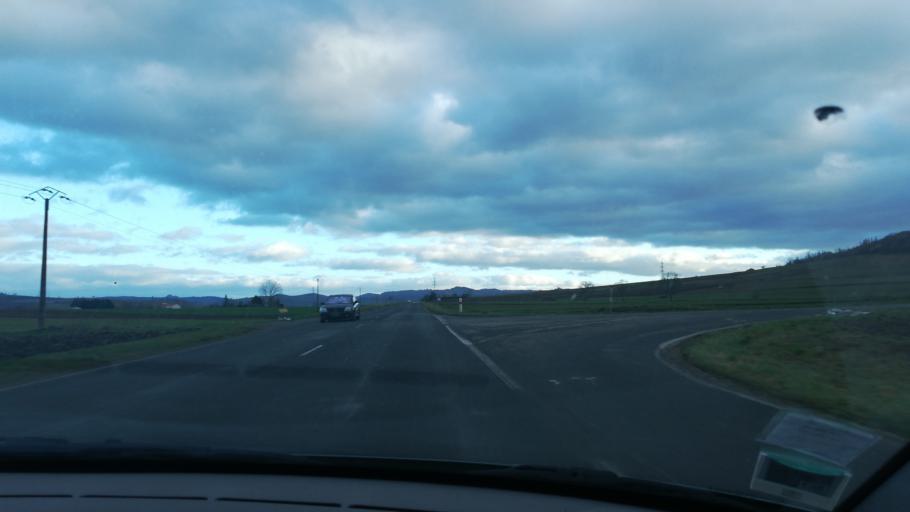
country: FR
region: Auvergne
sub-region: Departement du Puy-de-Dome
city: Vertaizon
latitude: 45.7534
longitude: 3.3178
